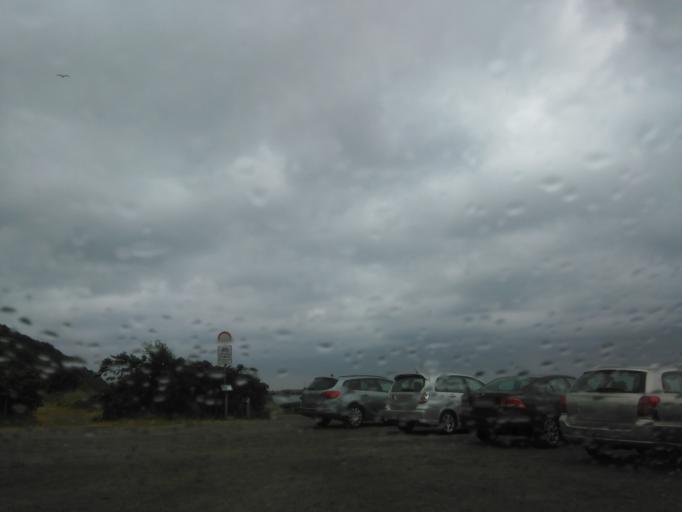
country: DK
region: Capital Region
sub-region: Bornholm Kommune
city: Ronne
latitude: 55.2478
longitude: 14.7352
